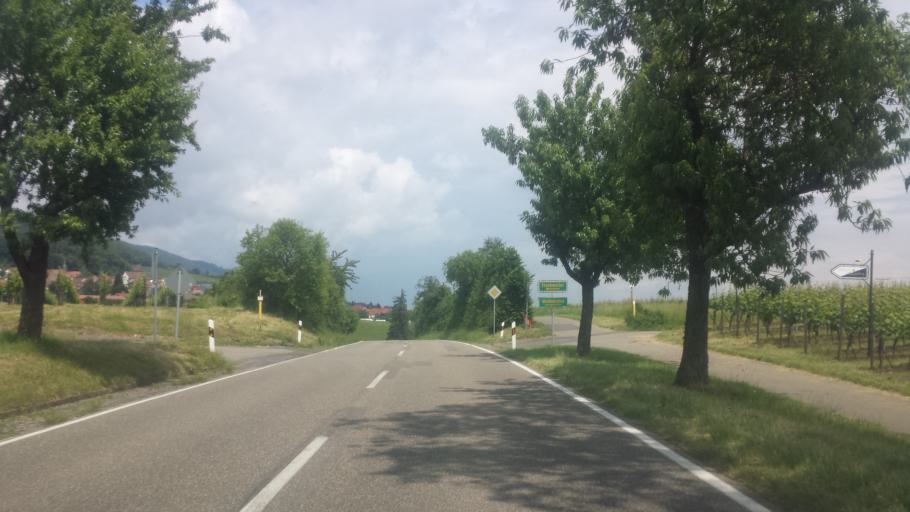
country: DE
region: Rheinland-Pfalz
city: Frankweiler
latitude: 49.2331
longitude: 8.0631
